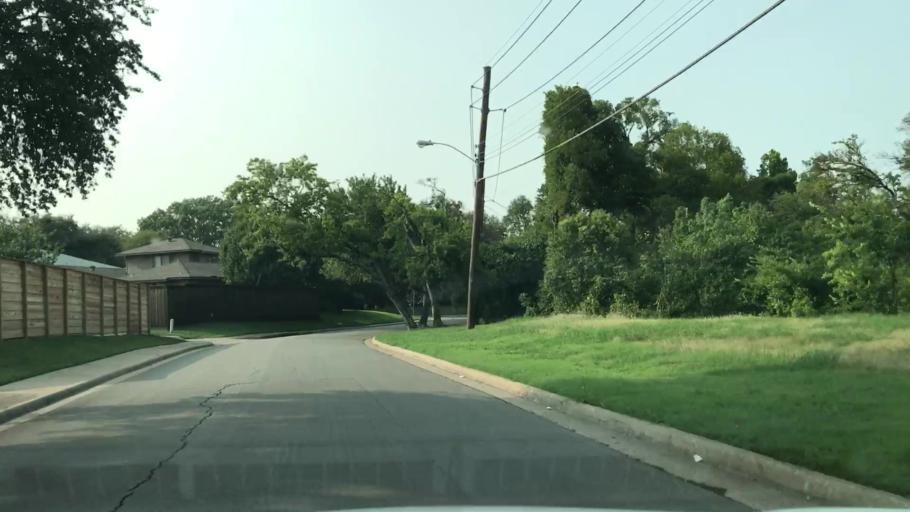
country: US
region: Texas
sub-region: Dallas County
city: Richardson
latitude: 32.9023
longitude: -96.7283
